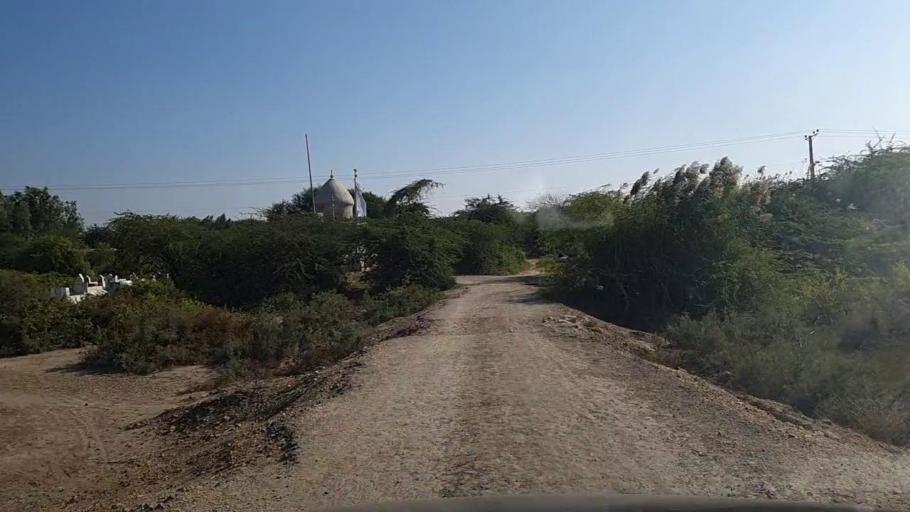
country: PK
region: Sindh
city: Mirpur Batoro
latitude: 24.7268
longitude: 68.2695
